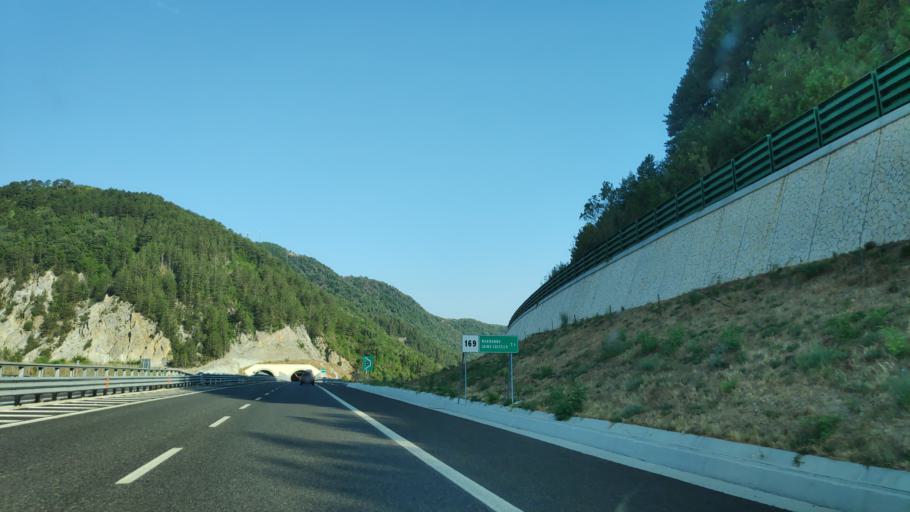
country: IT
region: Calabria
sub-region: Provincia di Cosenza
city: Mormanno
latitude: 39.8781
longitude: 15.9905
